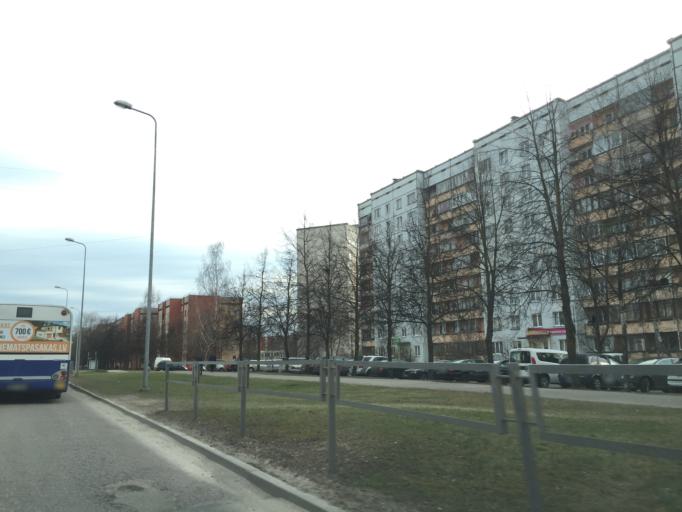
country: LV
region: Riga
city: Jaunciems
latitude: 56.9547
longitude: 24.1996
